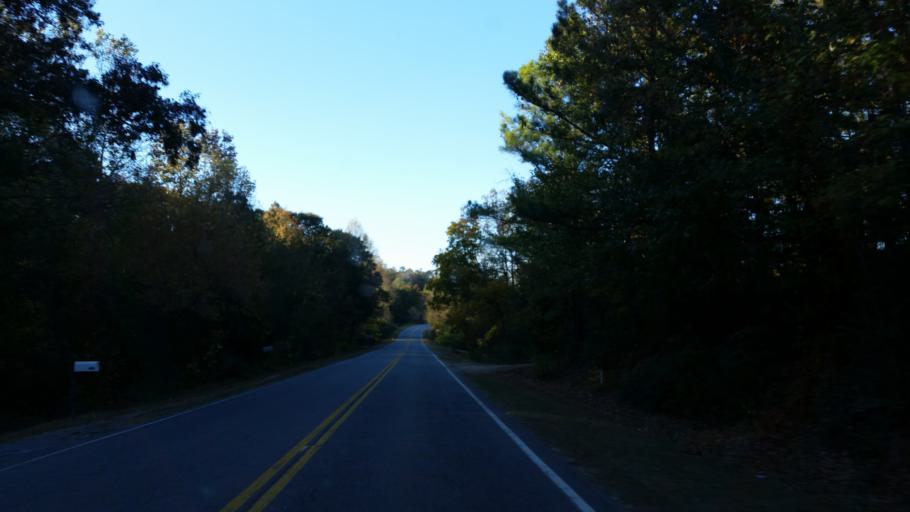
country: US
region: Georgia
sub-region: Bartow County
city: Adairsville
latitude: 34.3414
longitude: -84.9366
